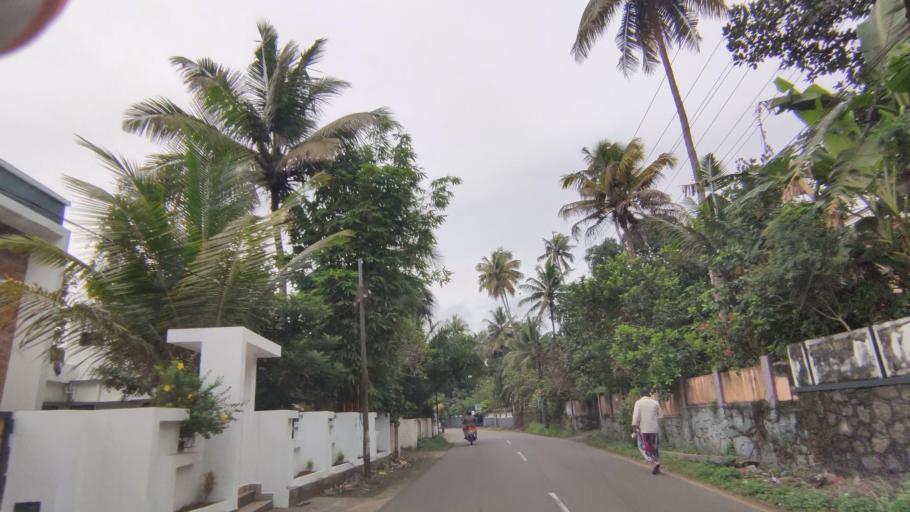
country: IN
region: Kerala
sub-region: Kottayam
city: Kottayam
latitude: 9.6768
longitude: 76.5057
